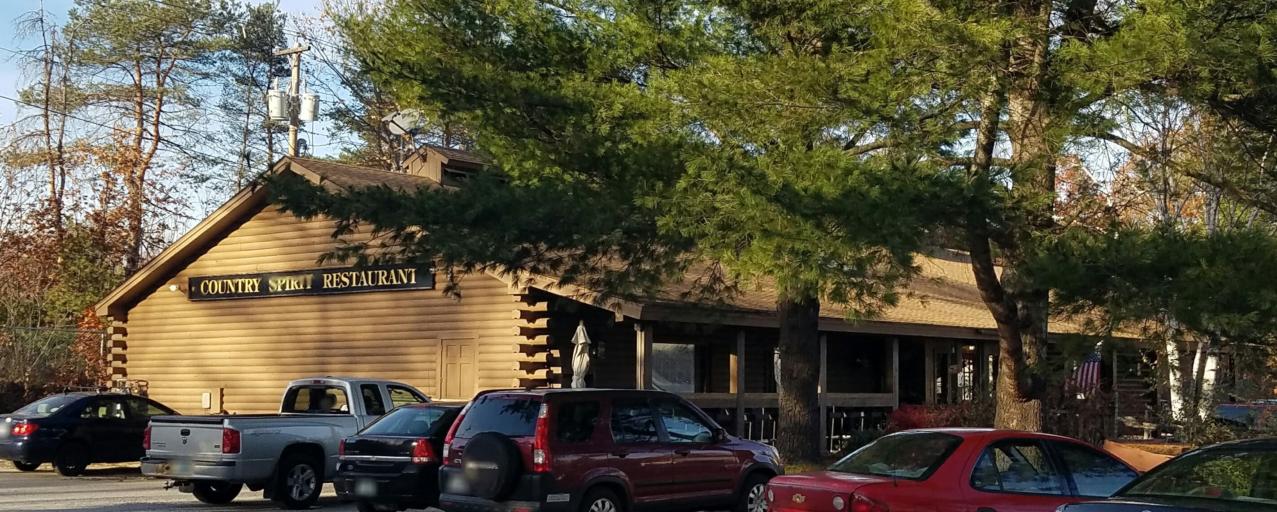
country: US
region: New Hampshire
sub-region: Merrimack County
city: Henniker
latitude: 43.1867
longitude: -71.8262
